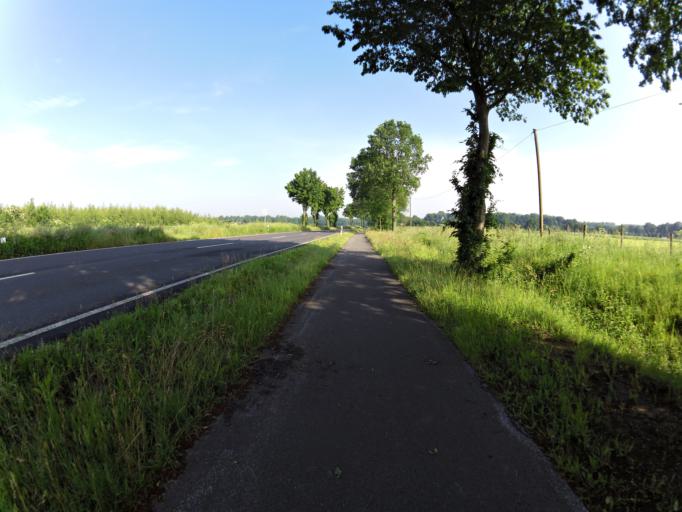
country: NL
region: Limburg
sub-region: Gemeente Sittard-Geleen
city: Sittard
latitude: 51.0428
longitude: 5.8716
